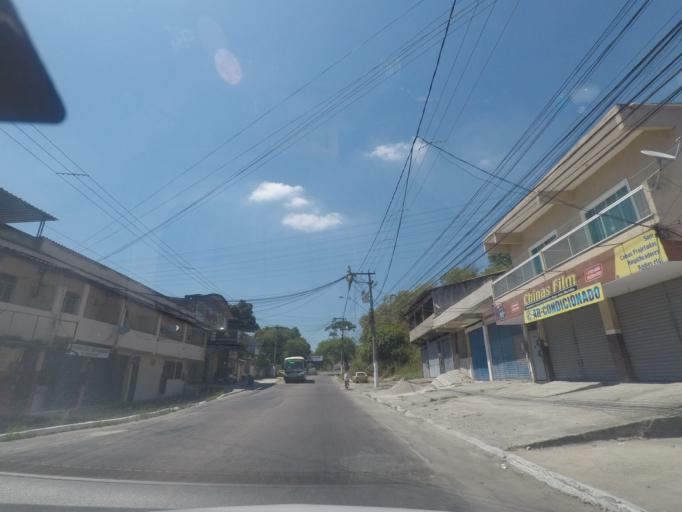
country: BR
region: Rio de Janeiro
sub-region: Petropolis
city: Petropolis
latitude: -22.5989
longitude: -43.1874
